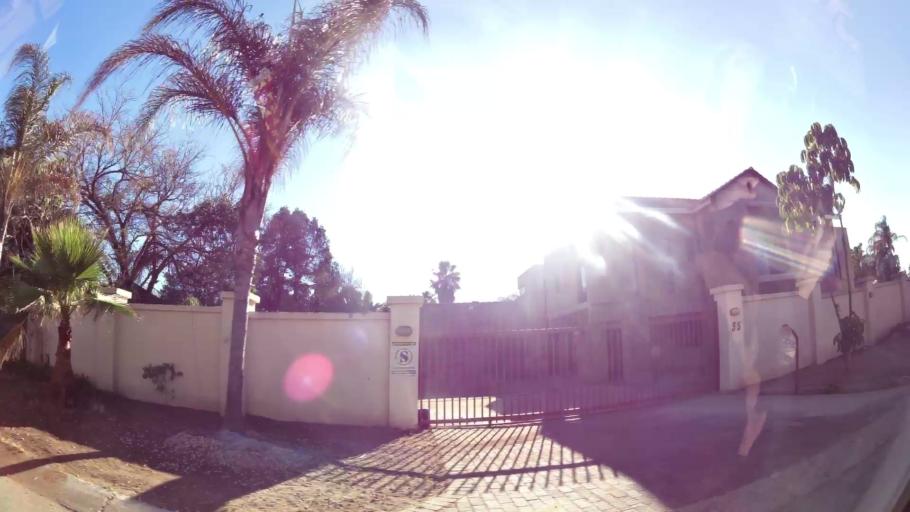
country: ZA
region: Limpopo
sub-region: Capricorn District Municipality
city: Polokwane
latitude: -23.8820
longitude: 29.4912
